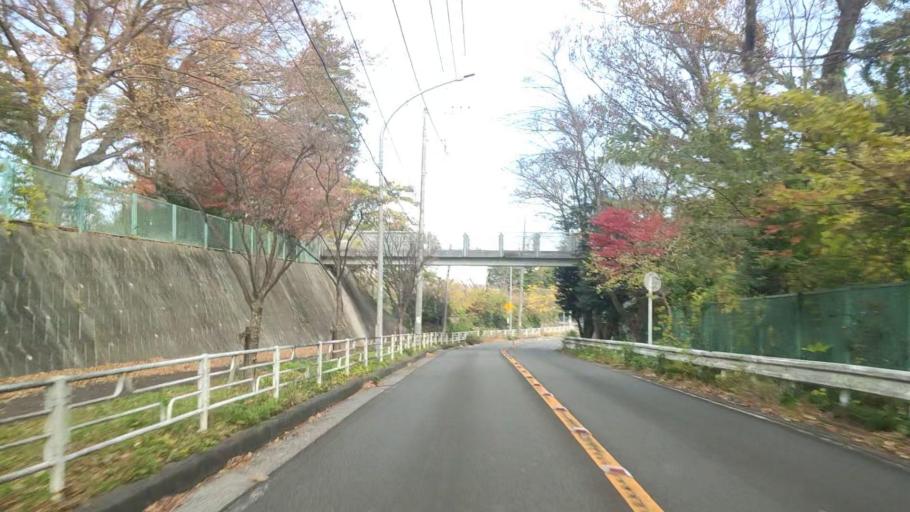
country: JP
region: Kanagawa
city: Minami-rinkan
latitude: 35.4498
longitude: 139.5385
